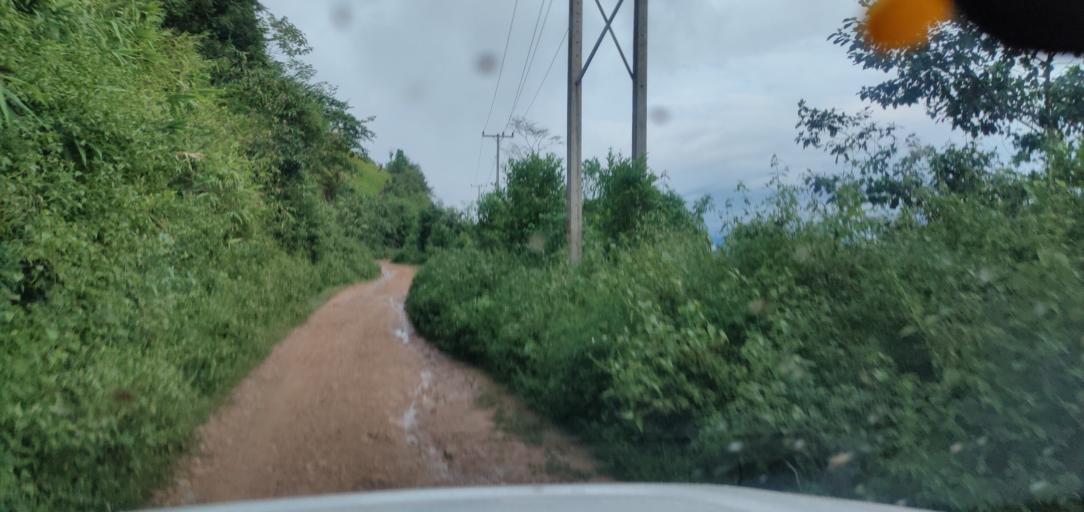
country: LA
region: Phongsali
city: Phongsali
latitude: 21.4483
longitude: 102.2867
